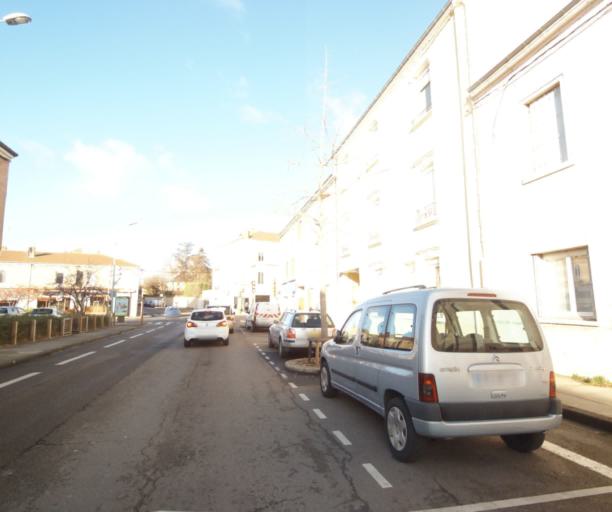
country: FR
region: Rhone-Alpes
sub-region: Departement de la Loire
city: Roanne
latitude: 46.0458
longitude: 4.0751
